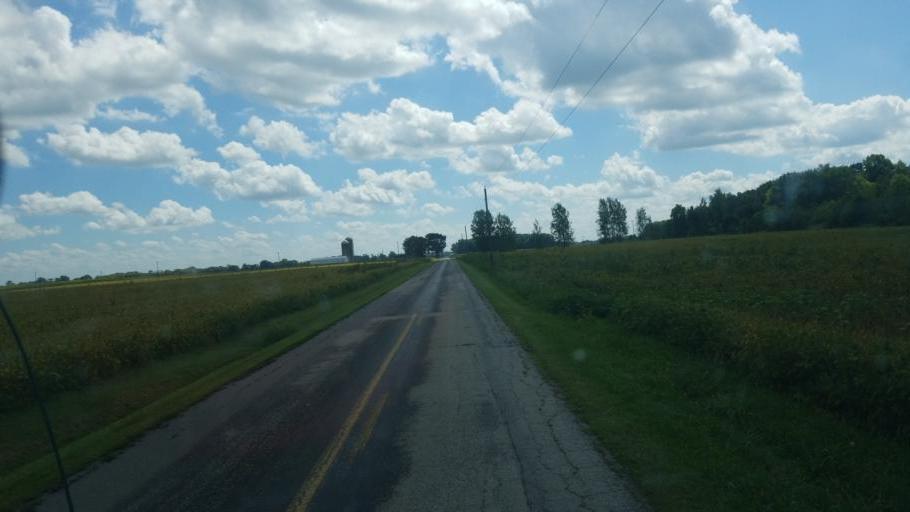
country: US
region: Ohio
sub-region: Marion County
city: Prospect
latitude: 40.4880
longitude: -83.1663
